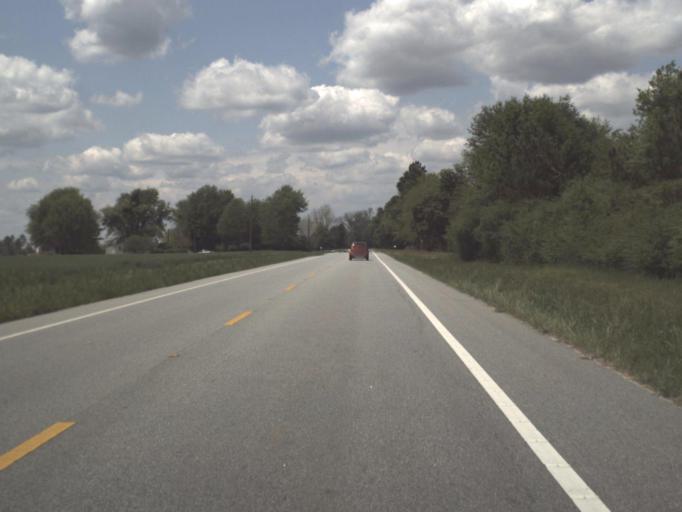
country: US
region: Alabama
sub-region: Escambia County
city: Atmore
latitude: 30.8908
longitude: -87.4656
